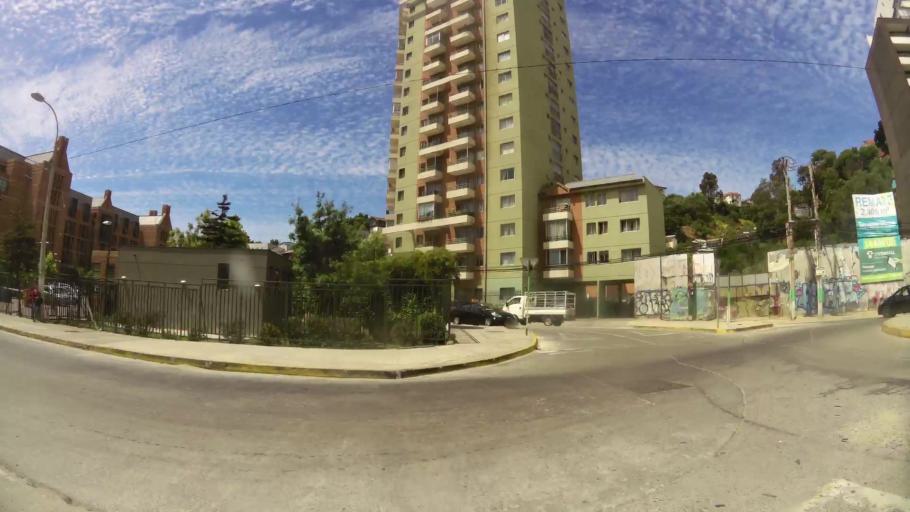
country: CL
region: Valparaiso
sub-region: Provincia de Valparaiso
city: Vina del Mar
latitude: -33.0340
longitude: -71.5889
